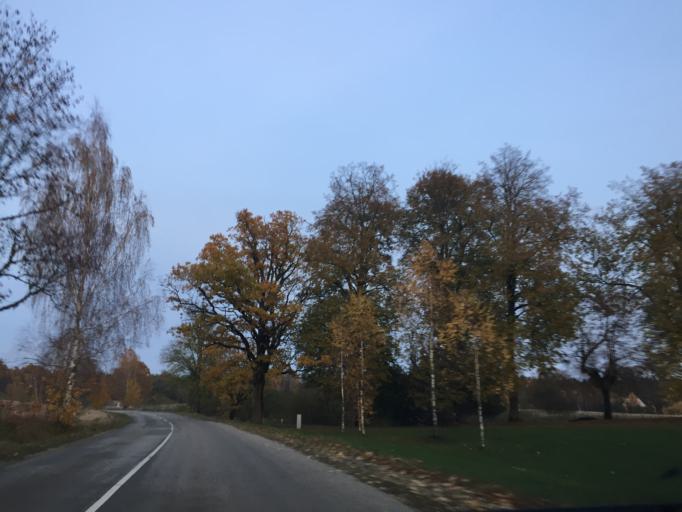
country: LV
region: Cesu Rajons
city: Cesis
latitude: 57.3158
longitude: 25.1936
